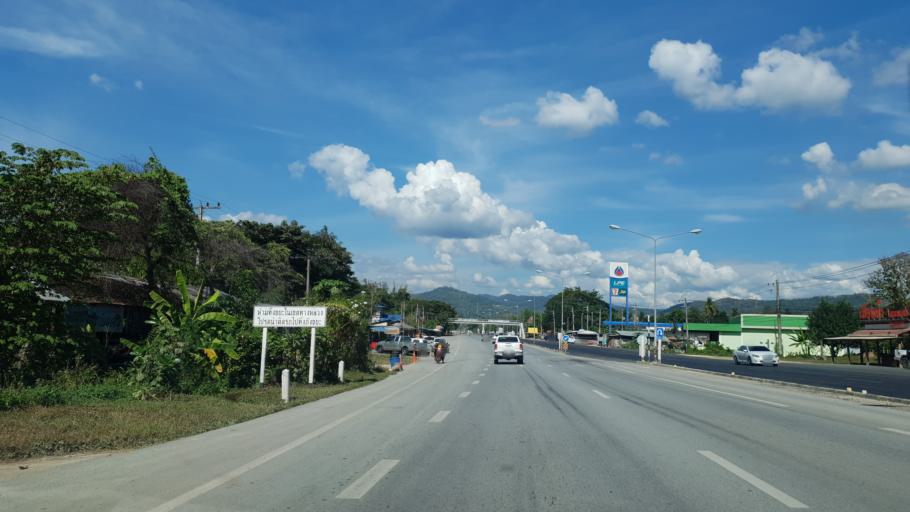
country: TH
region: Uttaradit
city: Uttaradit
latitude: 17.7419
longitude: 100.1331
